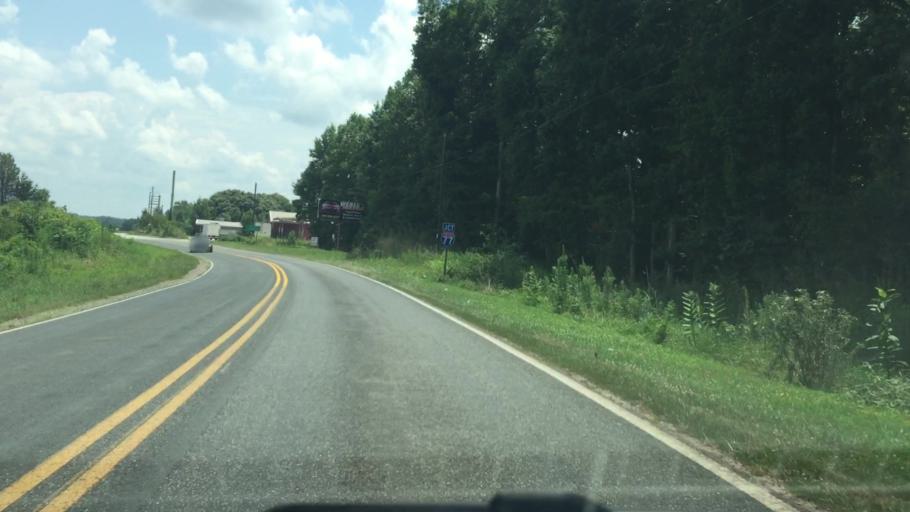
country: US
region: North Carolina
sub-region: Iredell County
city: Troutman
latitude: 35.7280
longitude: -80.8602
